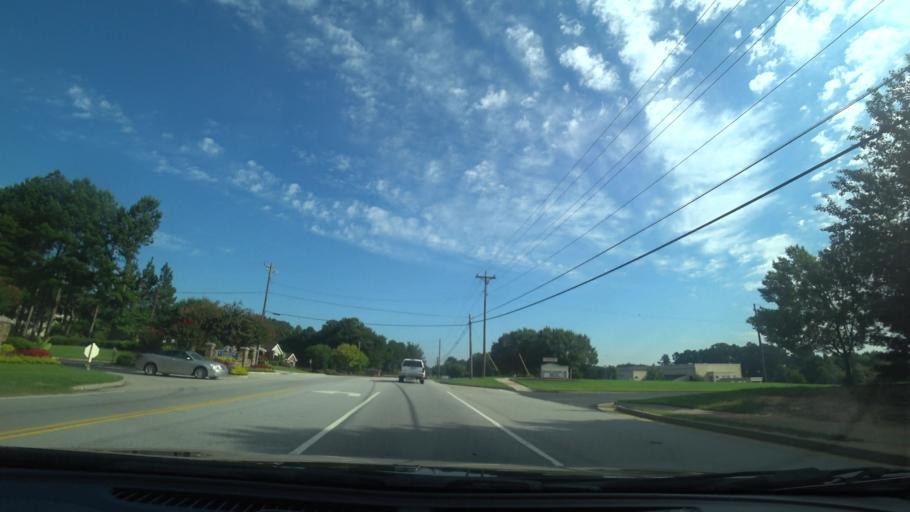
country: US
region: Georgia
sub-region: Gwinnett County
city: Grayson
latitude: 33.8644
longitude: -83.9571
